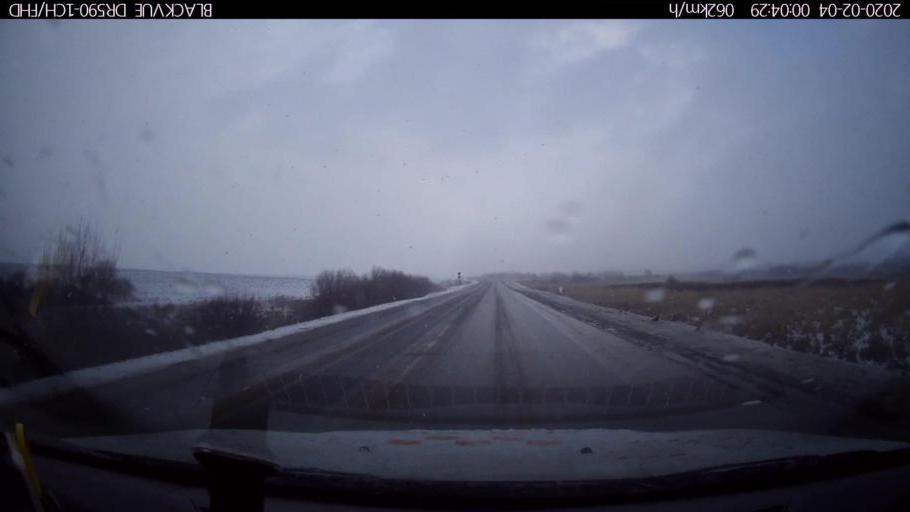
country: RU
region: Nizjnij Novgorod
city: Dal'neye Konstantinovo
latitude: 55.8270
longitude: 44.1188
